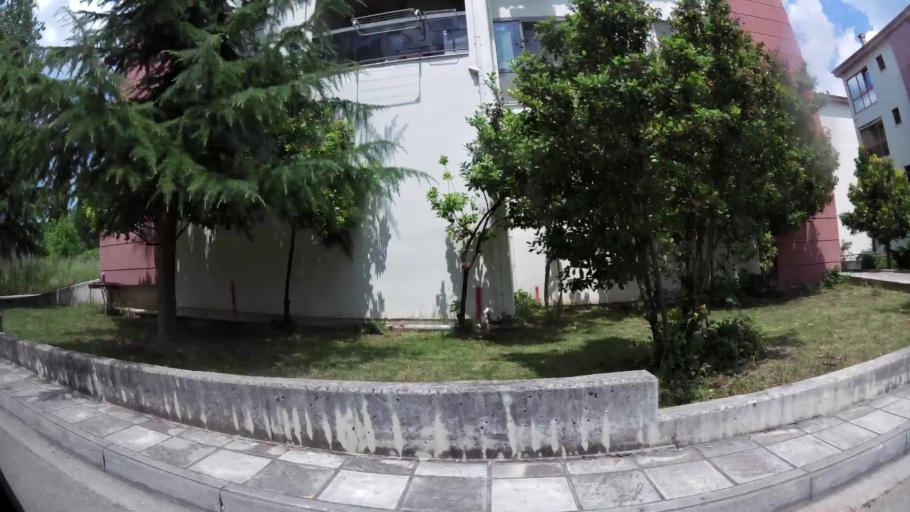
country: GR
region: West Macedonia
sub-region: Nomos Kozanis
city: Kozani
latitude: 40.2935
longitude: 21.7904
